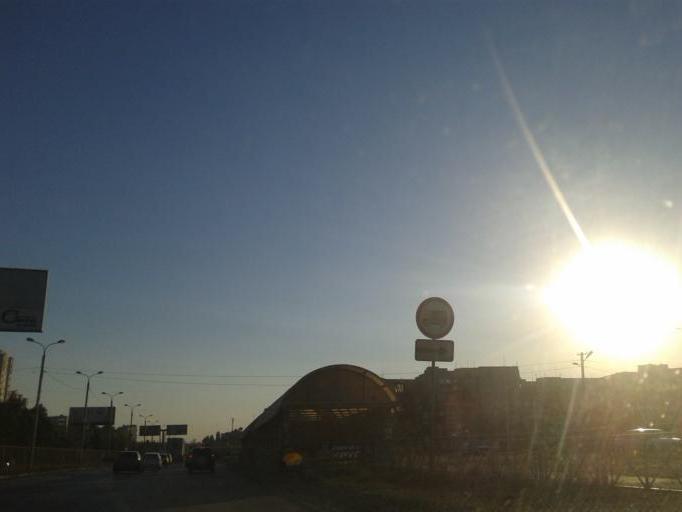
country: RU
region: Volgograd
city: Volgograd
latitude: 48.7598
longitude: 44.5012
